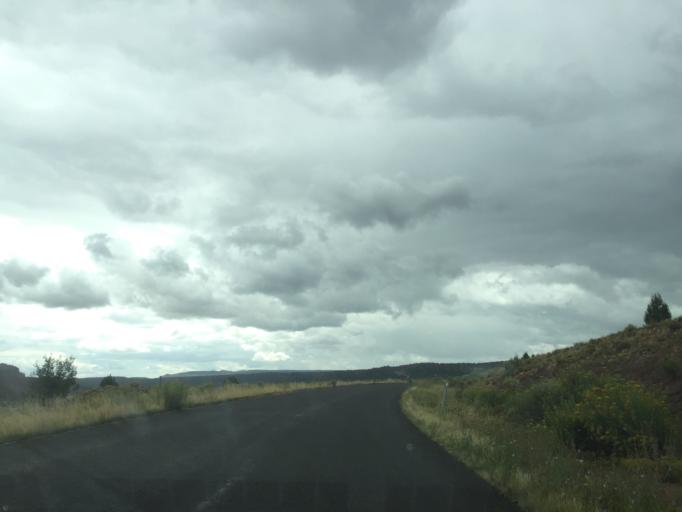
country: US
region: Utah
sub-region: Garfield County
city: Panguitch
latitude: 37.5436
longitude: -112.0447
